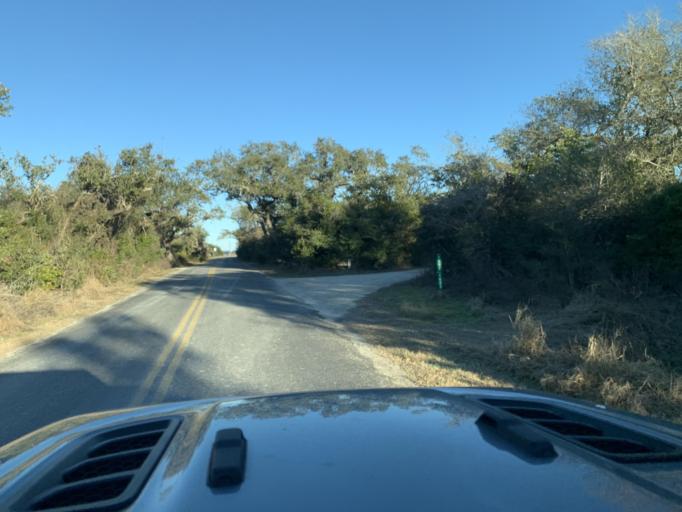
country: US
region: Texas
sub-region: Aransas County
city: Fulton
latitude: 28.1518
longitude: -96.9791
